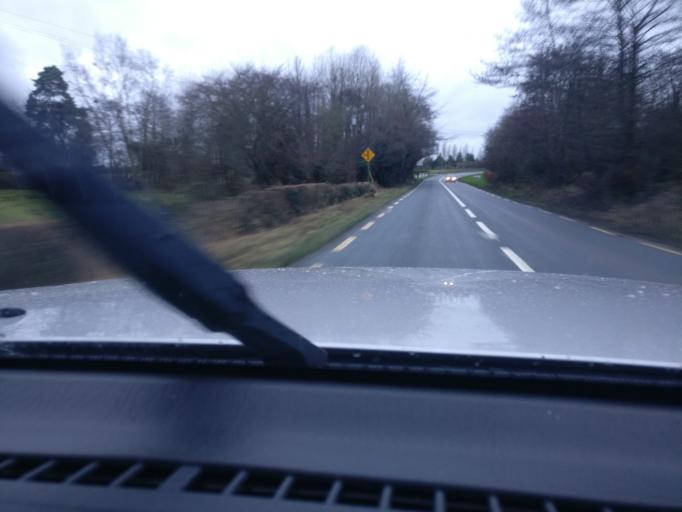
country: IE
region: Leinster
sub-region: An Mhi
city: Trim
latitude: 53.5228
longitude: -6.8219
